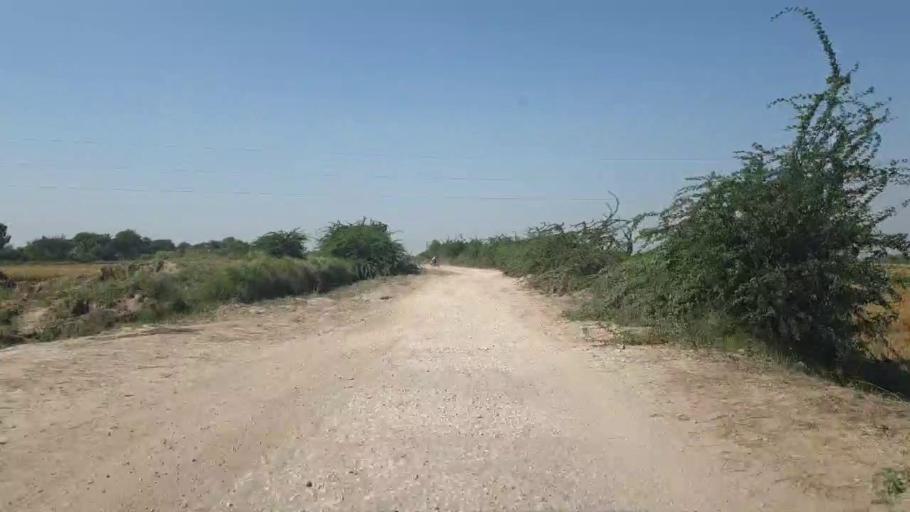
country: PK
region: Sindh
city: Talhar
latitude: 24.8346
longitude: 68.8108
